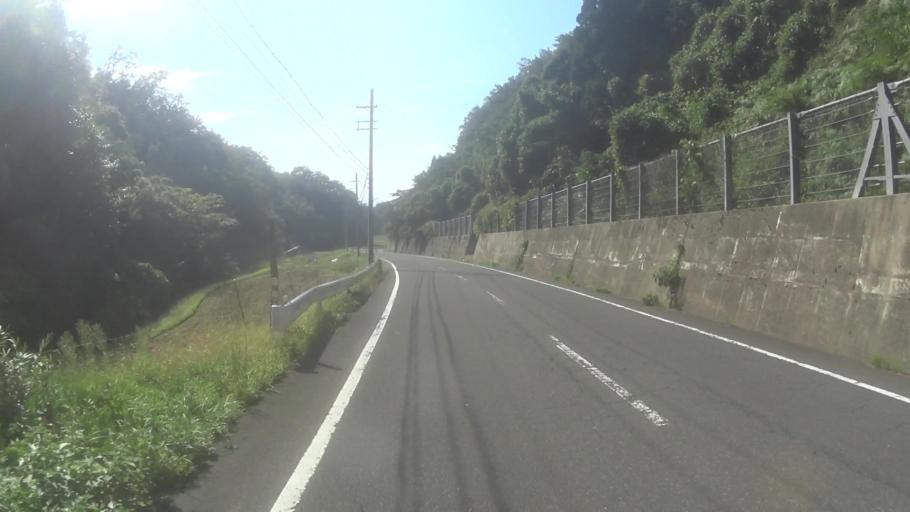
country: JP
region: Kyoto
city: Miyazu
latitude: 35.6919
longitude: 135.1302
